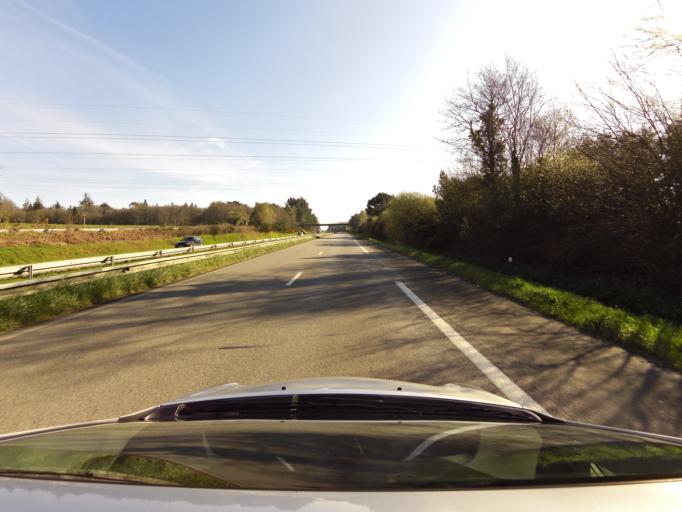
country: FR
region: Brittany
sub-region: Departement du Morbihan
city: Branderion
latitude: 47.8243
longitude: -3.2051
